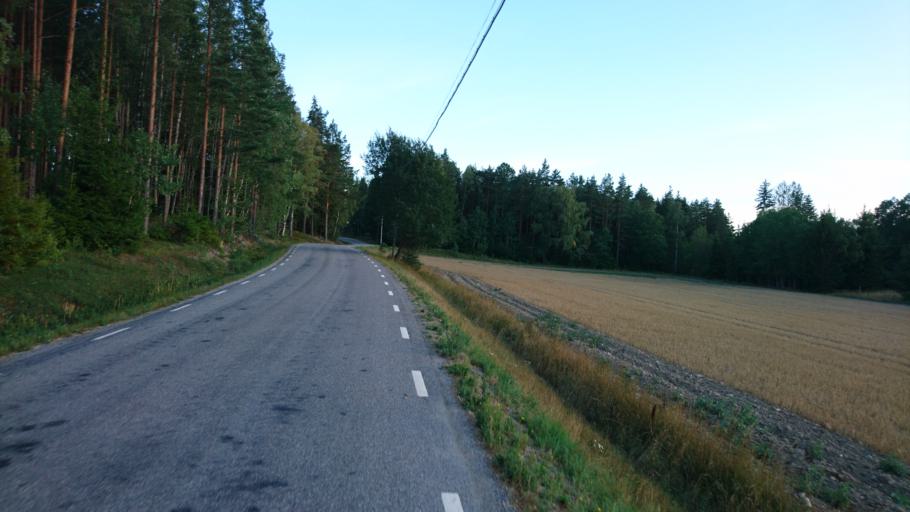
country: SE
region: Soedermanland
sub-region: Strangnas Kommun
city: Stallarholmen
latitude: 59.3936
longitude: 17.2681
